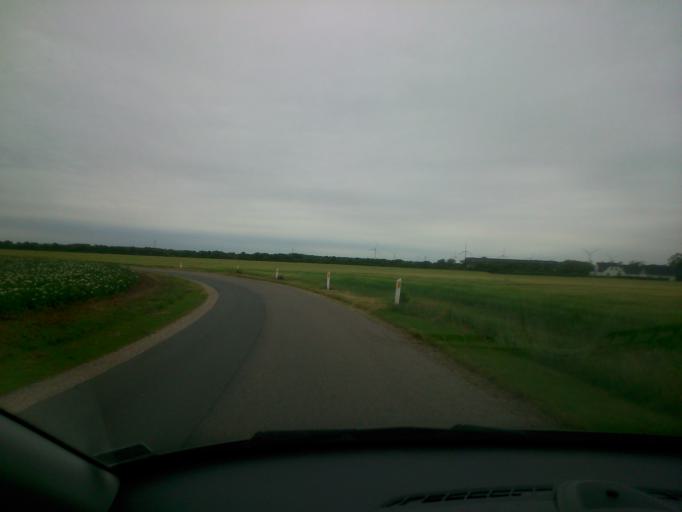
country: DK
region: Central Jutland
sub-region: Ringkobing-Skjern Kommune
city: Skjern
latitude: 55.9917
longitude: 8.3935
